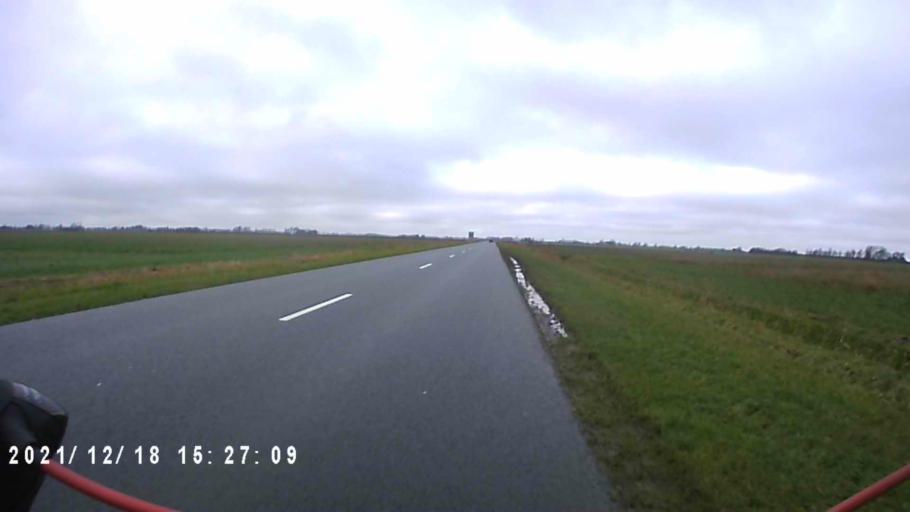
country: NL
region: Friesland
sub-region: Gemeente Dongeradeel
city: Anjum
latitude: 53.3287
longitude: 6.1479
